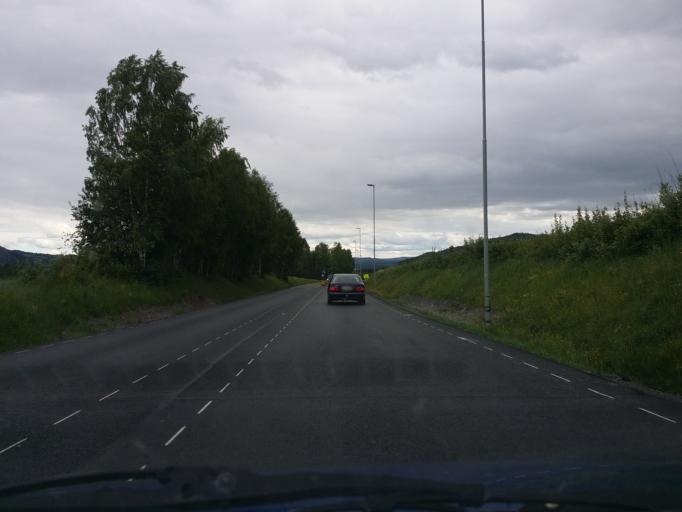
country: NO
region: Hedmark
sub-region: Ringsaker
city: Moelv
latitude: 60.9747
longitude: 10.5891
